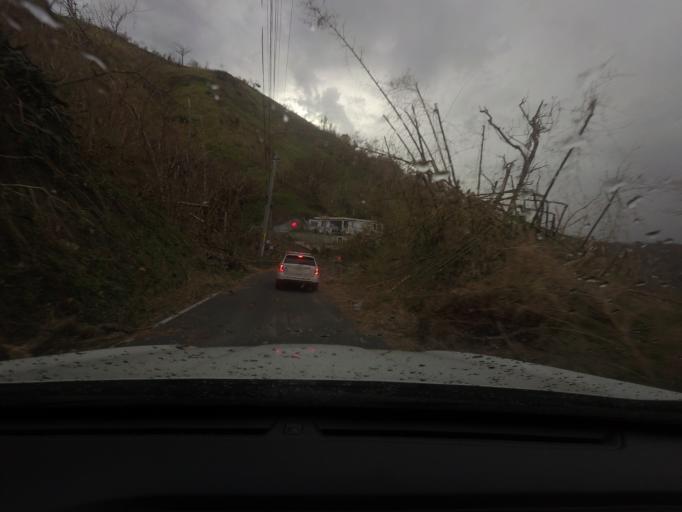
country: PR
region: Ciales
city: Ciales
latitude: 18.2846
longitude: -66.4792
